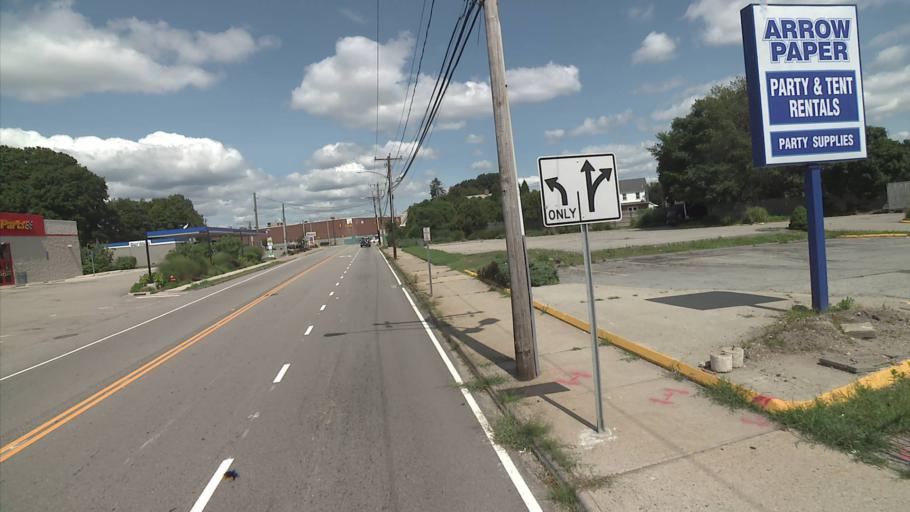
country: US
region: Connecticut
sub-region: New London County
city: New London
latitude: 41.3661
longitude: -72.1166
